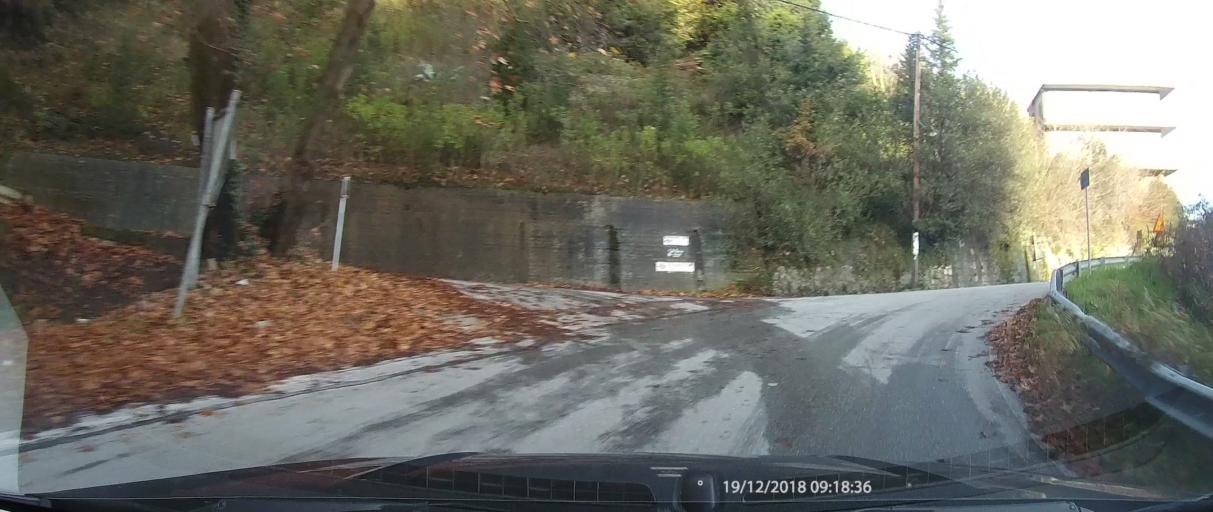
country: GR
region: Peloponnese
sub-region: Nomos Lakonias
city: Magoula
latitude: 37.0927
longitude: 22.3509
